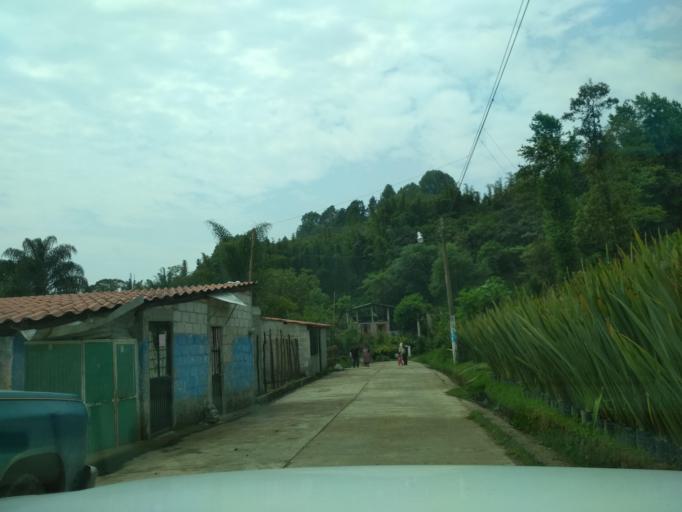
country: MX
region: Veracruz
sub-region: La Perla
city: La Perla
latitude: 18.9272
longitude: -97.1290
